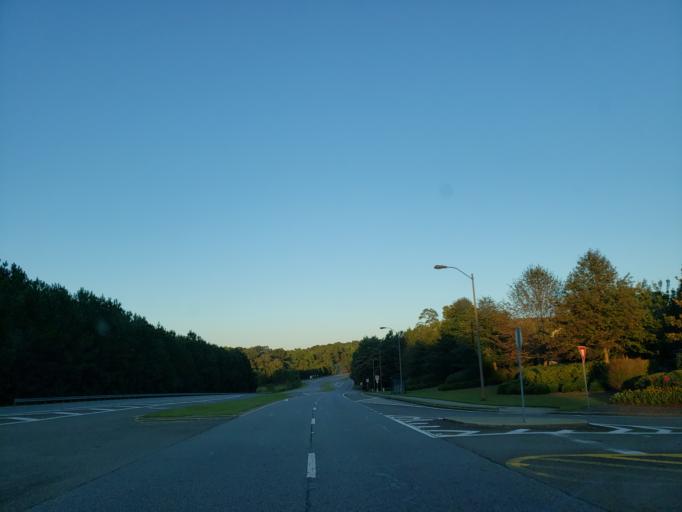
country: US
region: Georgia
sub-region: Cherokee County
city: Canton
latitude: 34.2575
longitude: -84.4897
